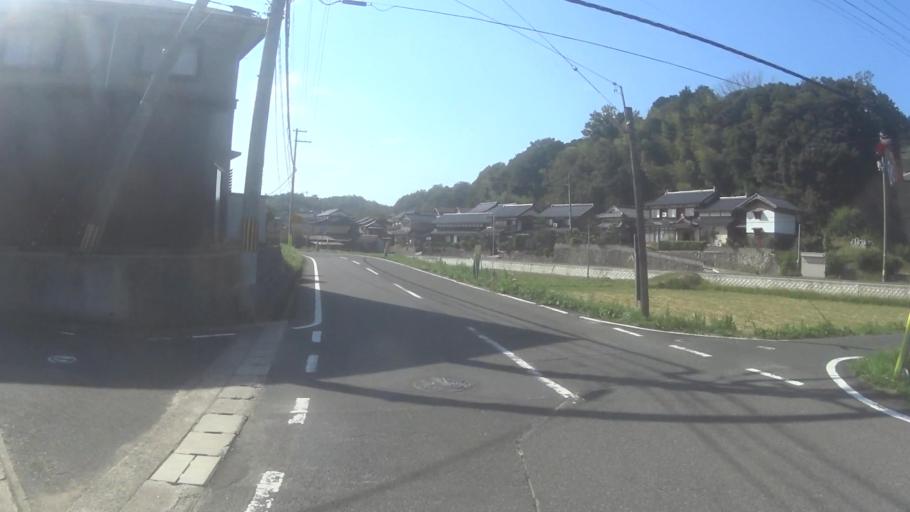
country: JP
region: Kyoto
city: Miyazu
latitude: 35.6822
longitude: 135.0924
